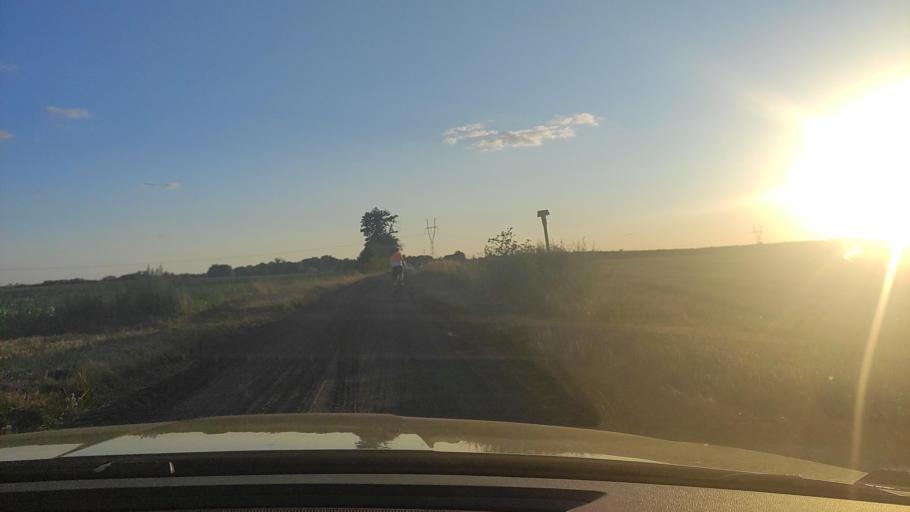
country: PL
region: Greater Poland Voivodeship
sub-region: Powiat poznanski
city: Kobylnica
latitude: 52.4552
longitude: 17.1415
